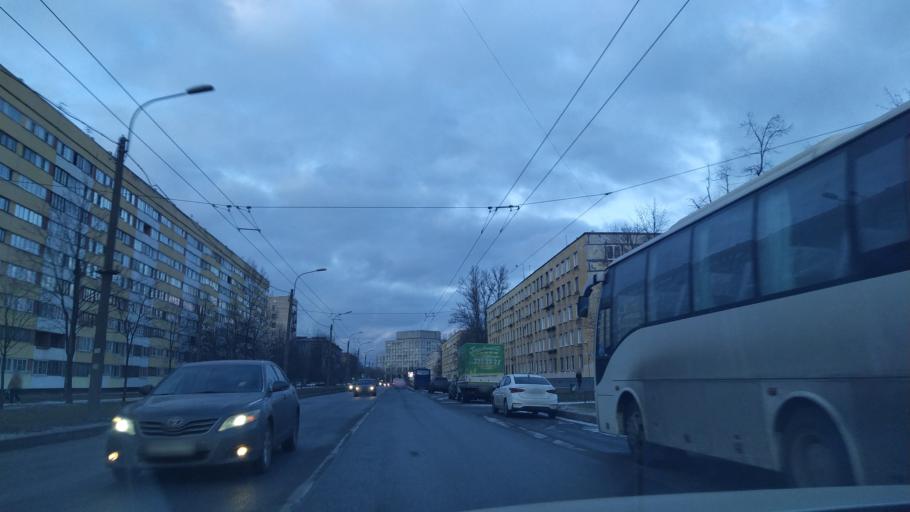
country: RU
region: St.-Petersburg
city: Dachnoye
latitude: 59.8531
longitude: 30.2563
